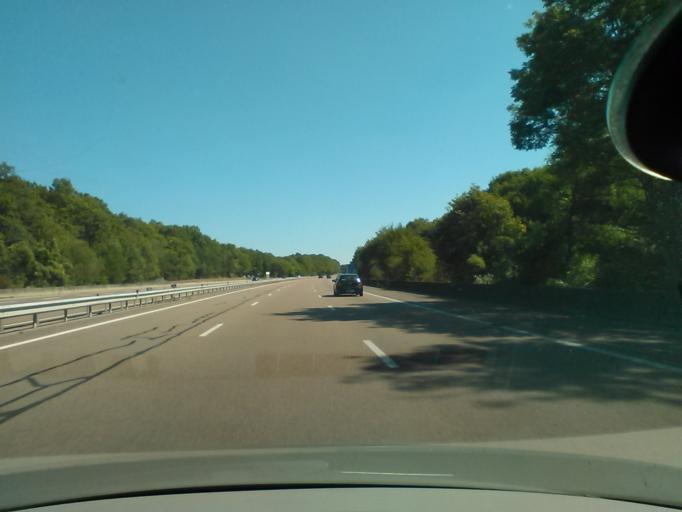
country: FR
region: Bourgogne
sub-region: Departement de l'Yonne
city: Aillant-sur-Tholon
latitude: 47.9219
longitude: 3.2832
